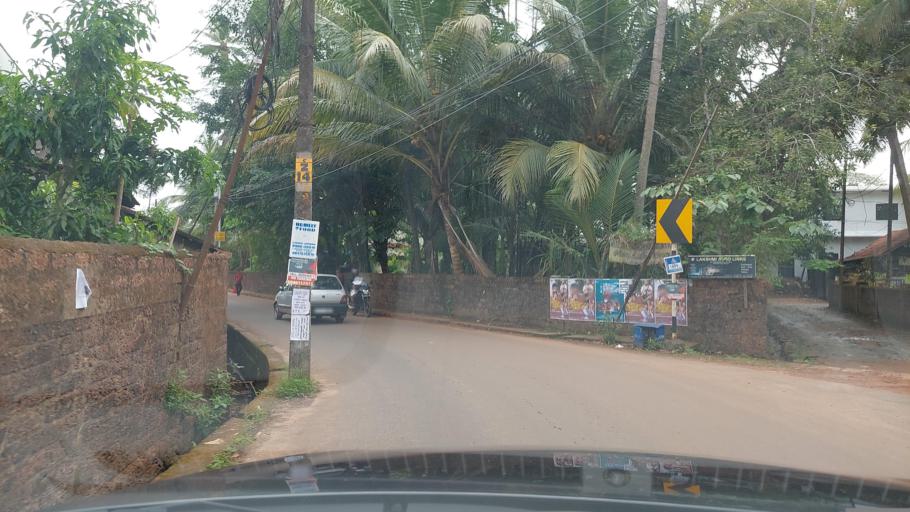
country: IN
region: Kerala
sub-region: Kozhikode
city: Kozhikode
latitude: 11.2496
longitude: 75.7883
